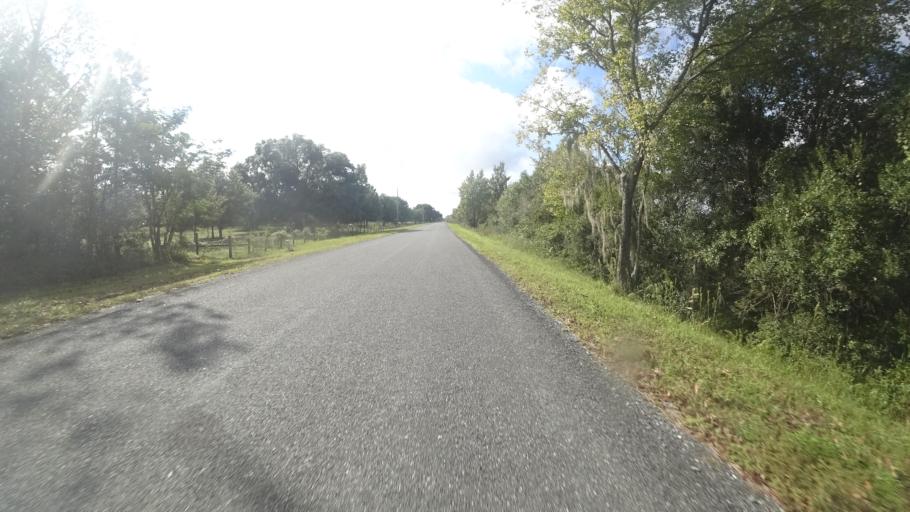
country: US
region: Florida
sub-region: Hillsborough County
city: Wimauma
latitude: 27.4695
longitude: -82.1533
